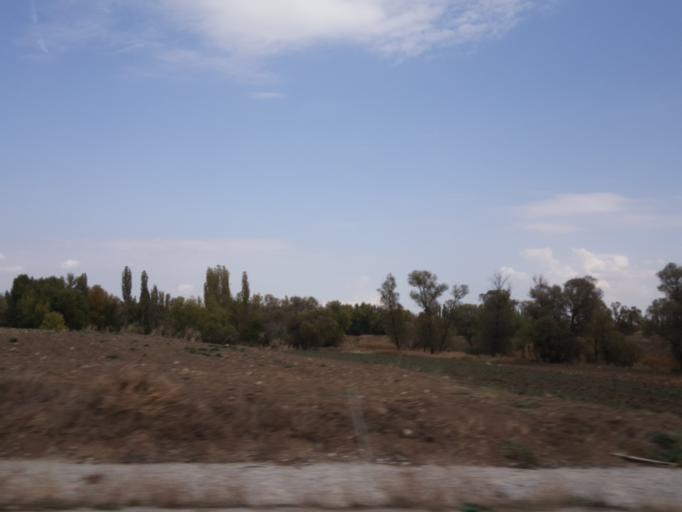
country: TR
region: Corum
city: Alaca
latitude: 40.1525
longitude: 34.7622
